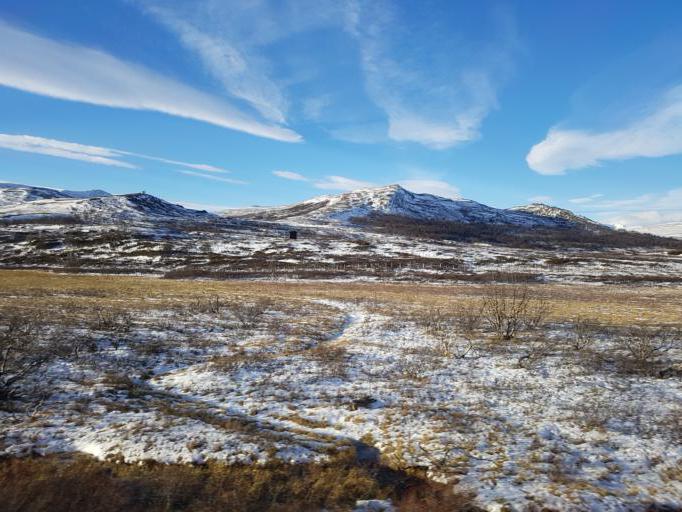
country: NO
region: Oppland
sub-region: Dovre
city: Dovre
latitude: 62.2320
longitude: 9.5402
